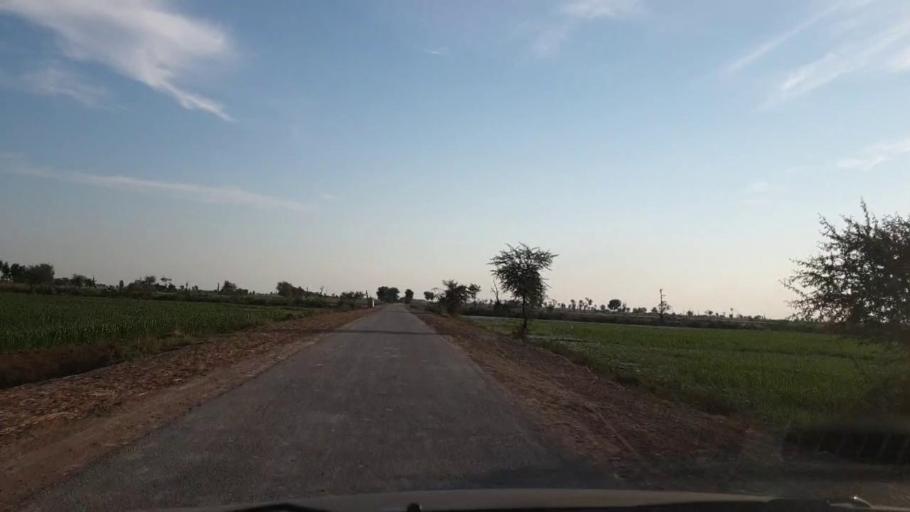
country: PK
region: Sindh
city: Khadro
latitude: 26.1657
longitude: 68.7531
